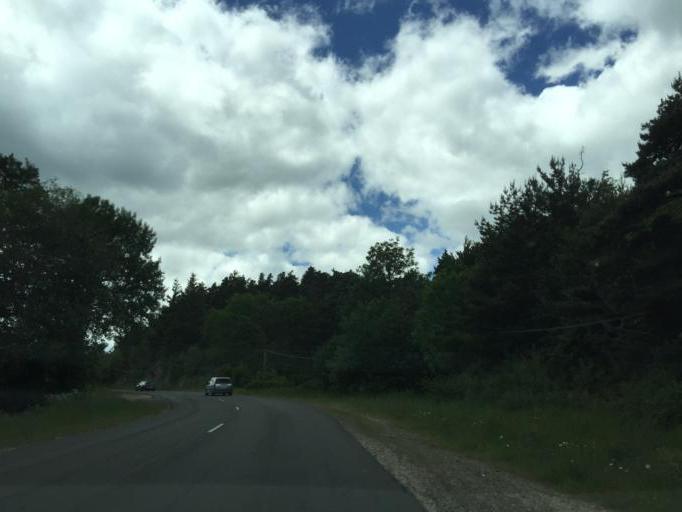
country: FR
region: Rhone-Alpes
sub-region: Departement de la Loire
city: Lezigneux
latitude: 45.5273
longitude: 4.0085
